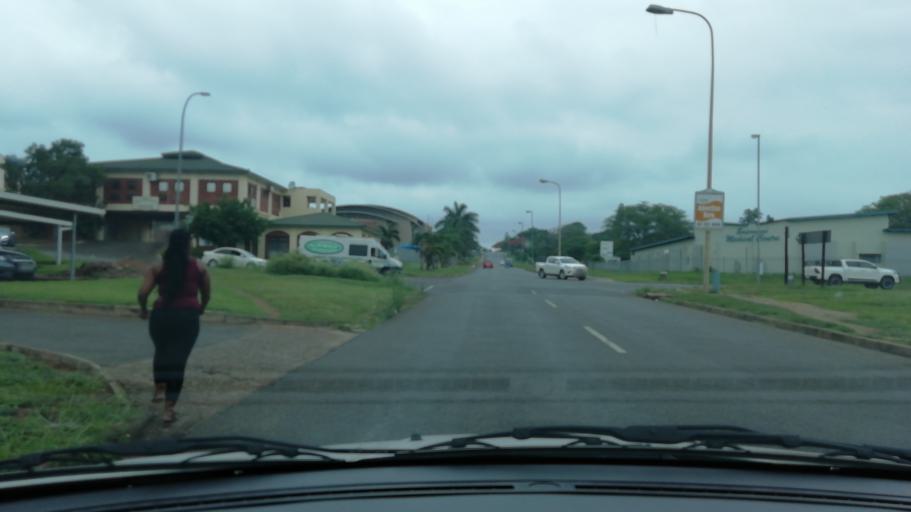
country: ZA
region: KwaZulu-Natal
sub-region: uThungulu District Municipality
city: Empangeni
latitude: -28.7368
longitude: 31.8934
